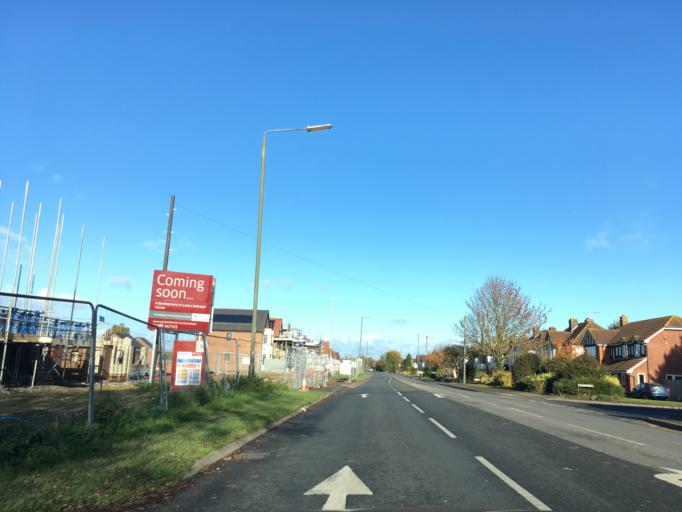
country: GB
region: England
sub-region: Worcestershire
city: Evesham
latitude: 52.0751
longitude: -1.9536
